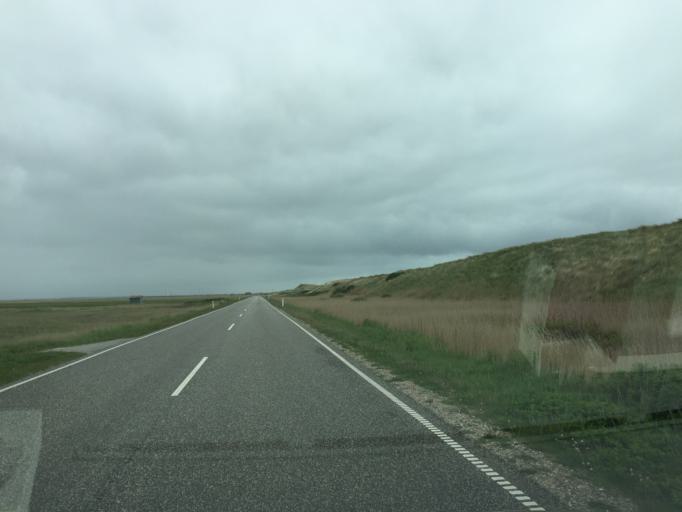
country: DK
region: Central Jutland
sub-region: Lemvig Kommune
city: Harboore
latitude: 56.4071
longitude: 8.1223
